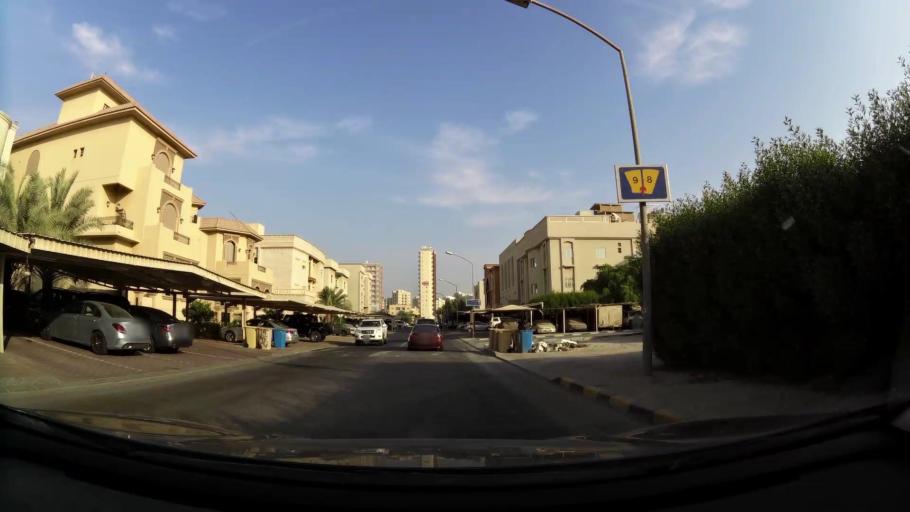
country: KW
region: Muhafazat Hawalli
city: Ar Rumaythiyah
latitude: 29.3226
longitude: 48.0723
